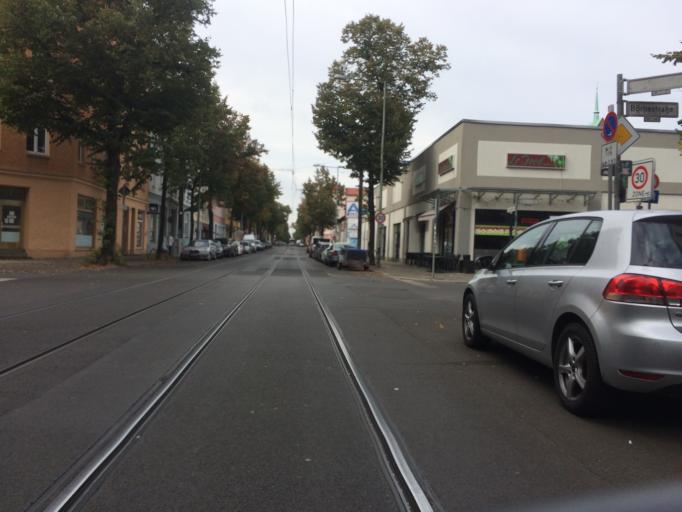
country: DE
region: Berlin
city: Weissensee
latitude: 52.5493
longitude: 13.4485
